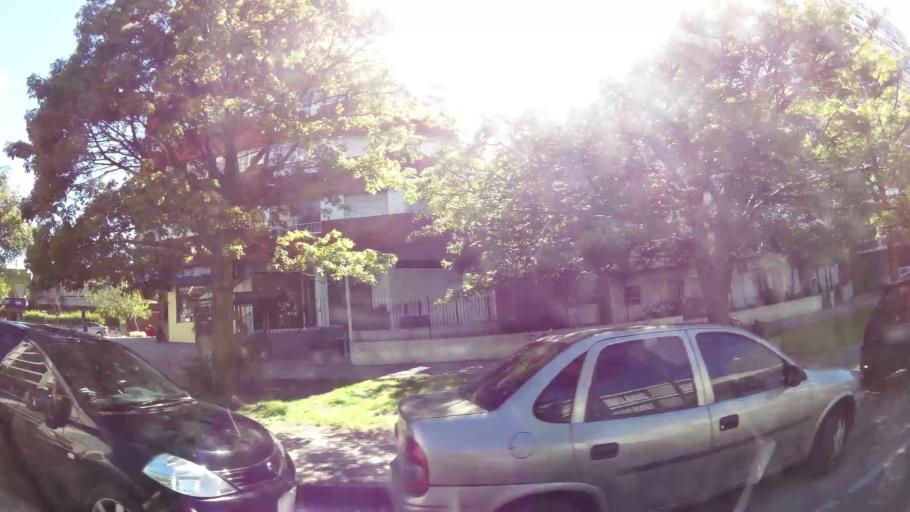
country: UY
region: Montevideo
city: Montevideo
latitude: -34.8900
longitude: -56.1598
